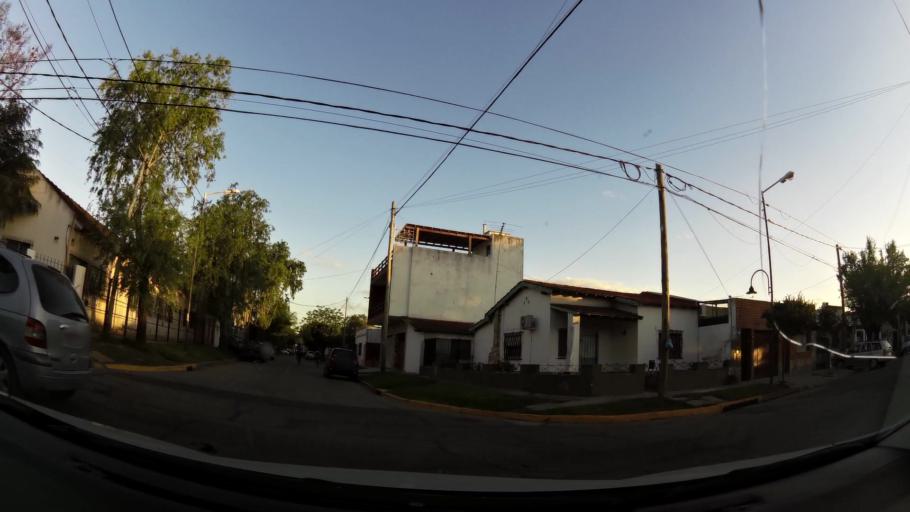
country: AR
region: Buenos Aires
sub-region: Partido de Tigre
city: Tigre
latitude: -34.4434
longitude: -58.5710
